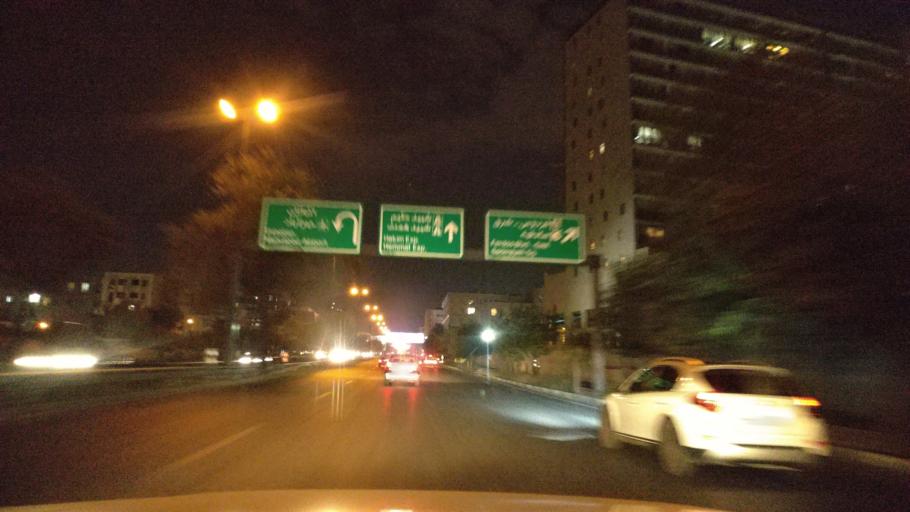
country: IR
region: Tehran
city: Tehran
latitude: 35.7197
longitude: 51.3079
